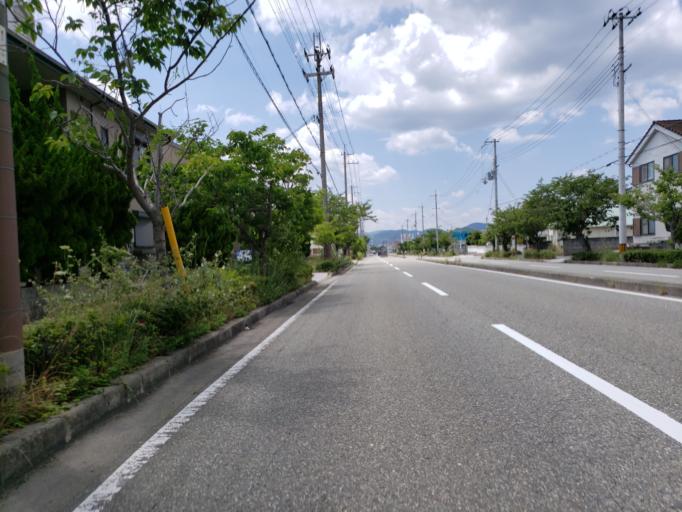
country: JP
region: Hyogo
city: Kariya
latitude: 34.7388
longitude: 134.4014
